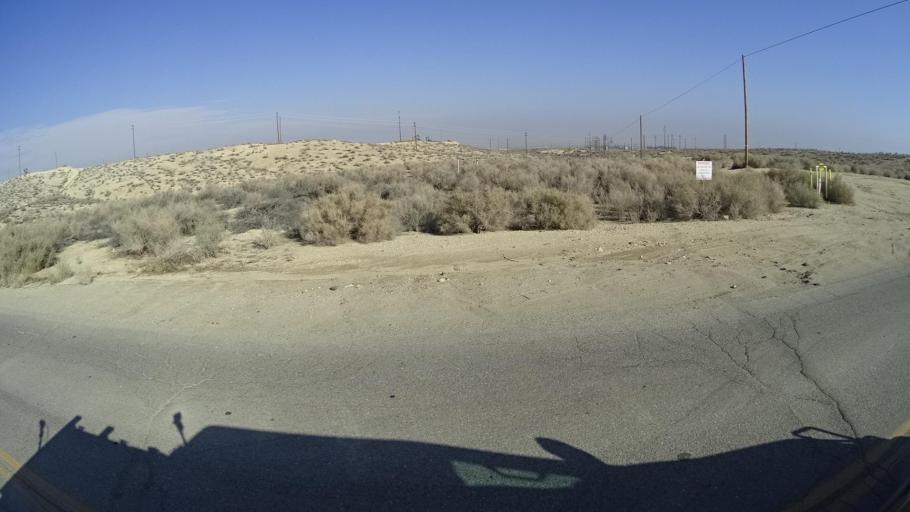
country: US
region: California
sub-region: Kern County
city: Taft Heights
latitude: 35.1430
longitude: -119.5062
